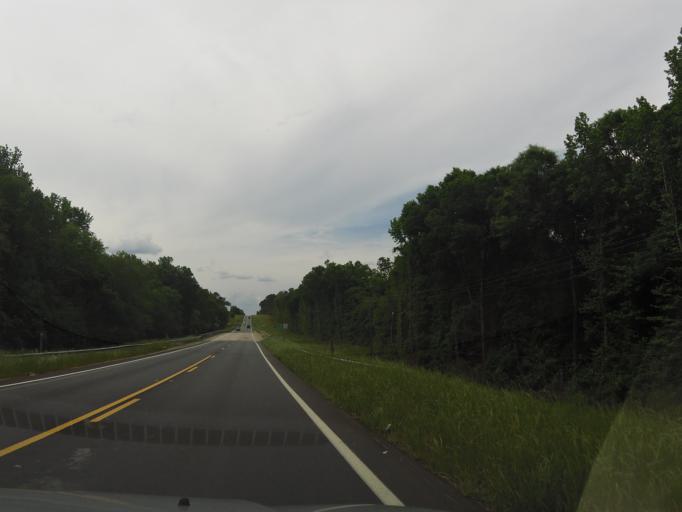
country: US
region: Georgia
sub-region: McDuffie County
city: Thomson
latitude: 33.3390
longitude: -82.4574
